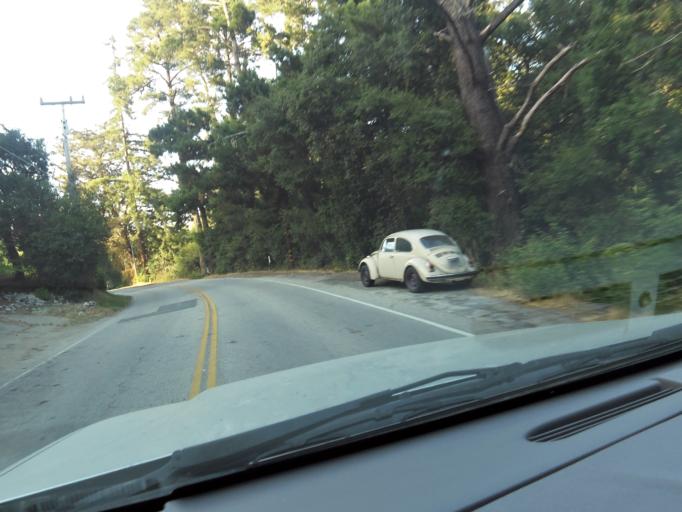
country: US
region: California
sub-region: Santa Cruz County
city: Pasatiempo
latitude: 37.0084
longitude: -122.0020
